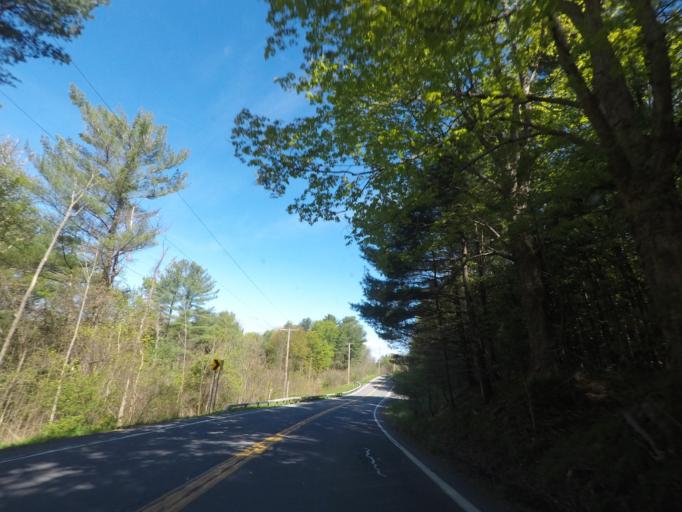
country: US
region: New York
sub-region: Albany County
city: Ravena
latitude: 42.5003
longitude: -73.9454
